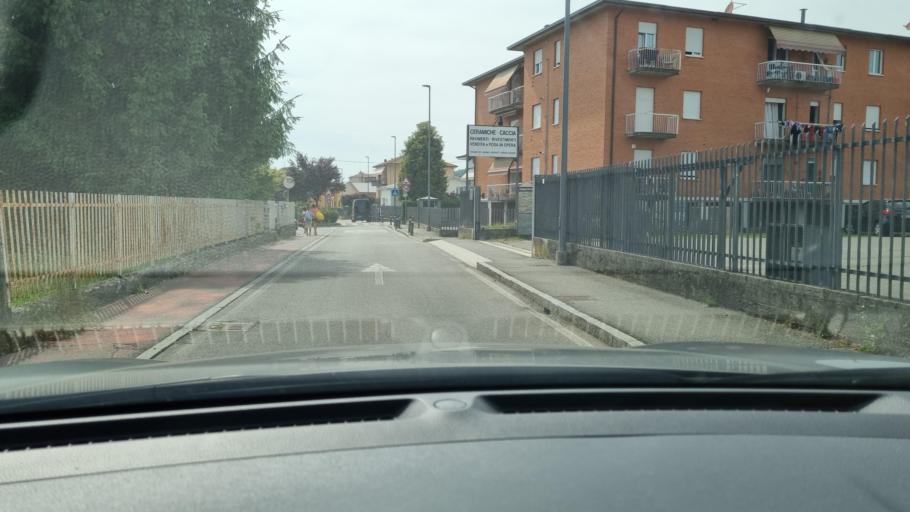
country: IT
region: Lombardy
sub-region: Provincia di Bergamo
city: Mapello
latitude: 45.7090
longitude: 9.5537
